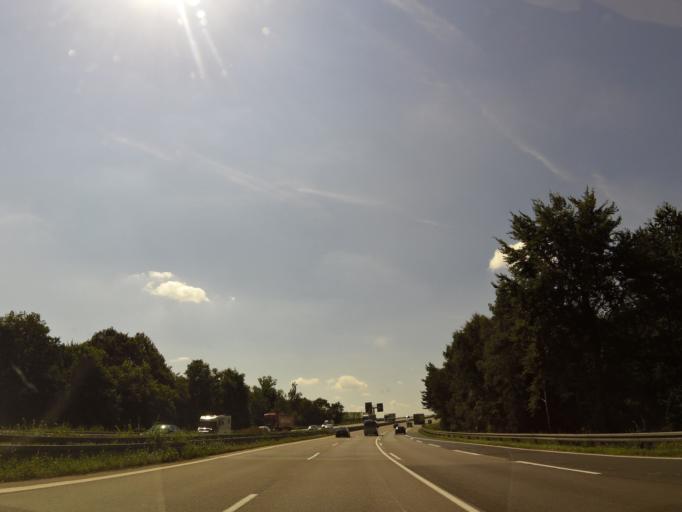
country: DE
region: Bavaria
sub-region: Upper Bavaria
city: Wolnzach
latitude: 48.5792
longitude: 11.5911
